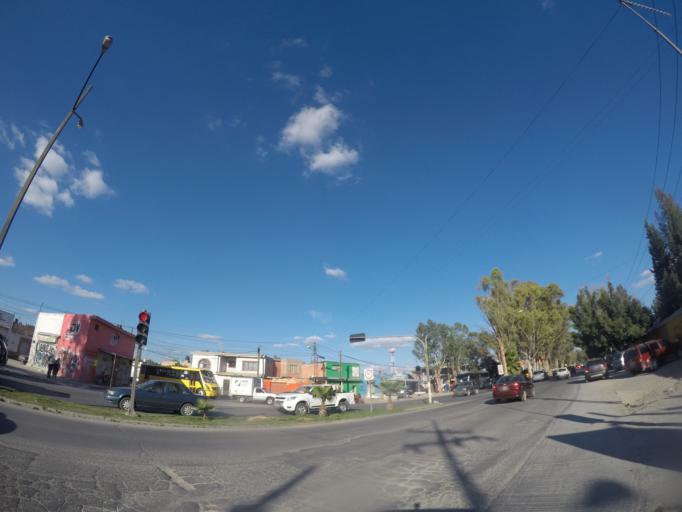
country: MX
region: San Luis Potosi
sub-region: San Luis Potosi
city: San Luis Potosi
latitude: 22.1833
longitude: -101.0011
